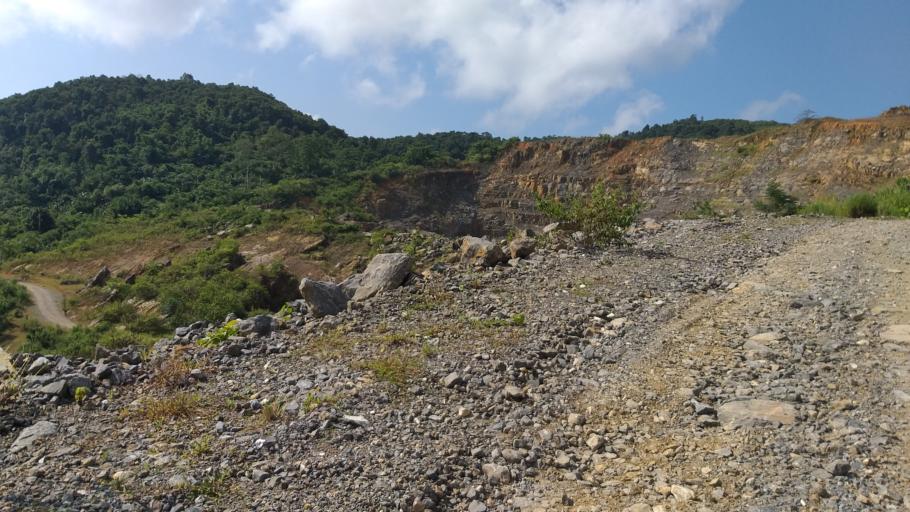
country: LA
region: Phongsali
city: Khoa
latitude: 21.2212
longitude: 102.5992
